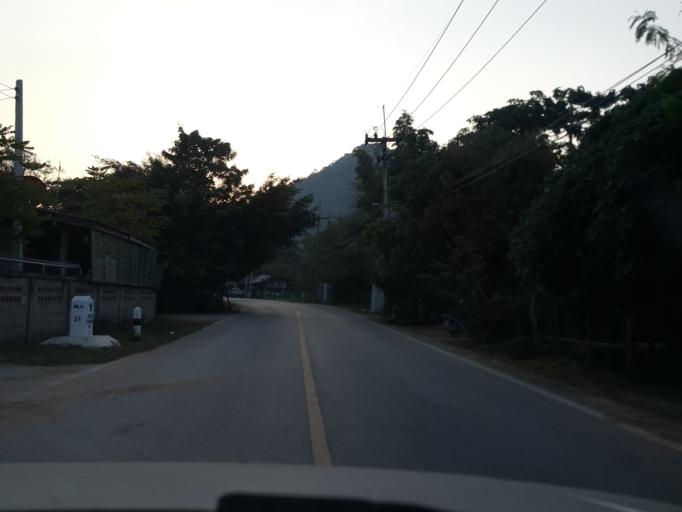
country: TH
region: Lamphun
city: Ban Thi
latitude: 18.5876
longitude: 99.2645
